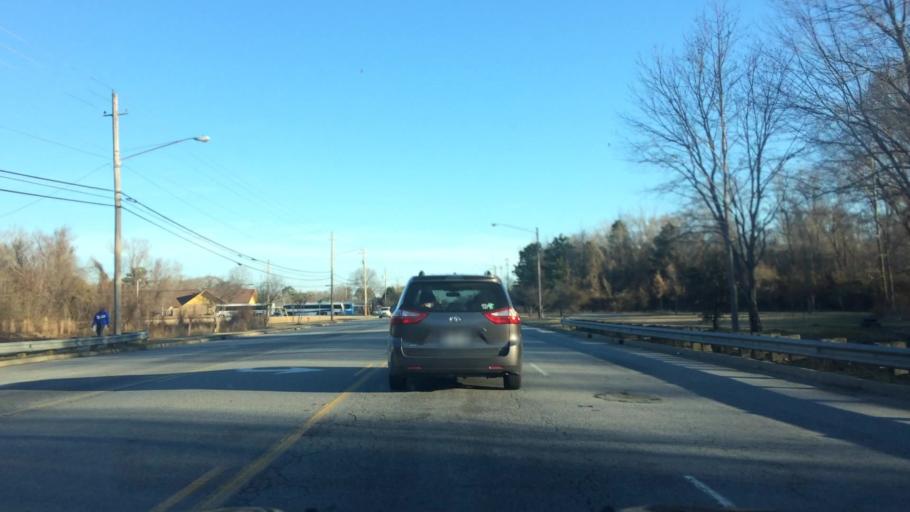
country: US
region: North Carolina
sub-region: Pitt County
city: Greenville
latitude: 35.5928
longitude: -77.3777
